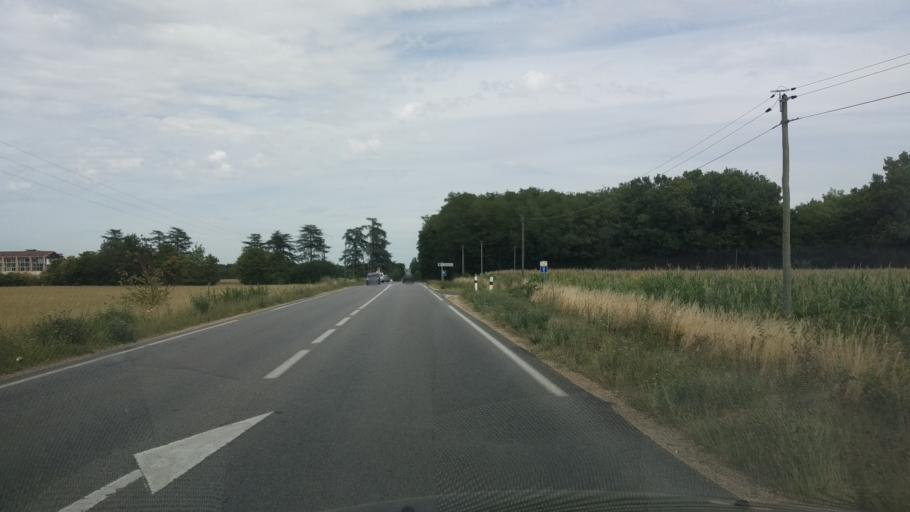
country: FR
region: Poitou-Charentes
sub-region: Departement de la Vienne
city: Mignaloux-Beauvoir
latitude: 46.5627
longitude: 0.4177
